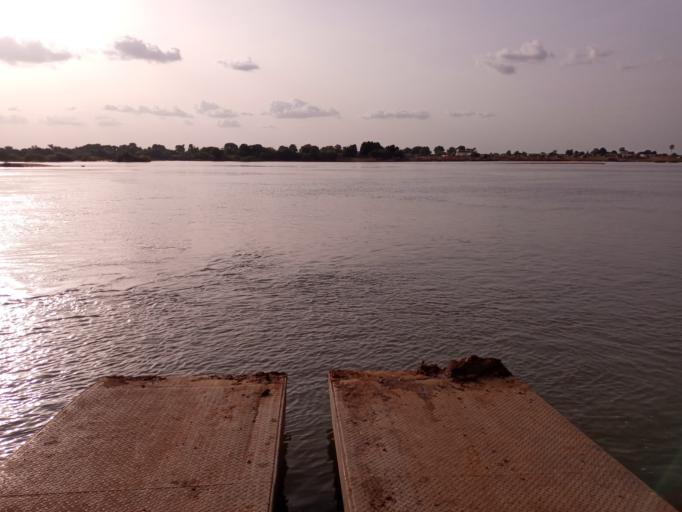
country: ML
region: Koulikoro
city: Kangaba
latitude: 12.1612
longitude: -8.2435
